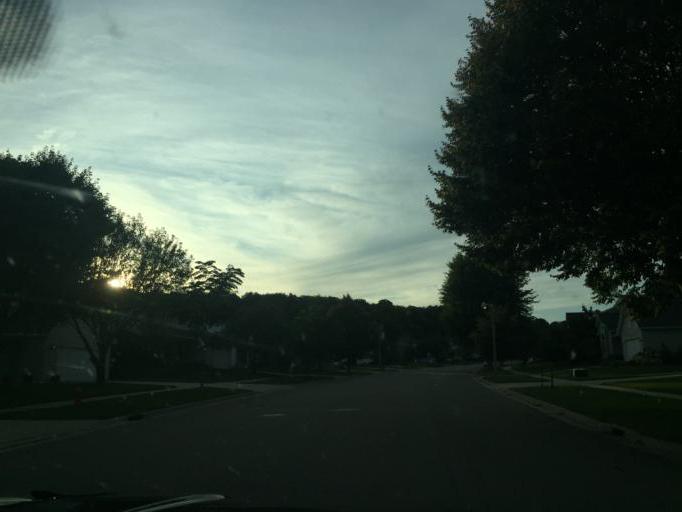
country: US
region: Minnesota
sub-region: Olmsted County
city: Rochester
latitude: 44.0056
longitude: -92.4892
